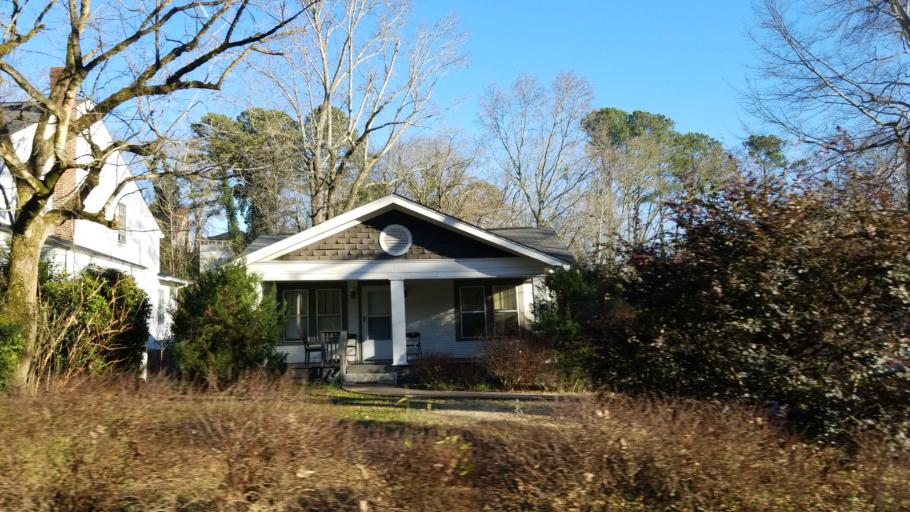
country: US
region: Tennessee
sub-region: Hamilton County
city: East Ridge
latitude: 35.0289
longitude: -85.2469
